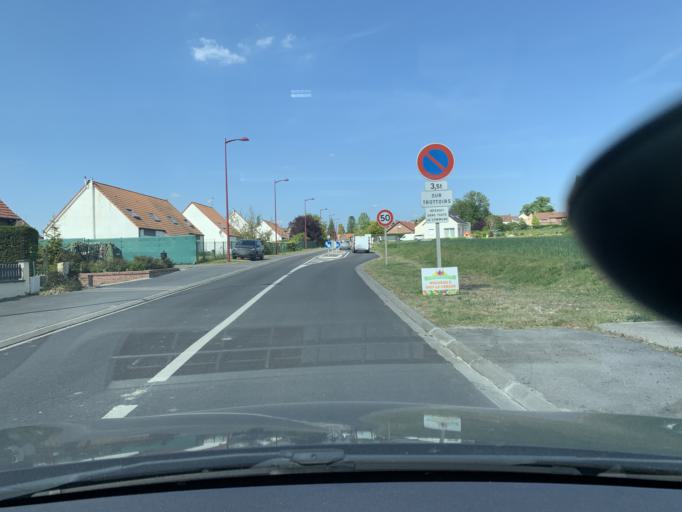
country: FR
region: Nord-Pas-de-Calais
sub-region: Departement du Pas-de-Calais
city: Oisy-le-Verger
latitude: 50.2438
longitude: 3.1166
